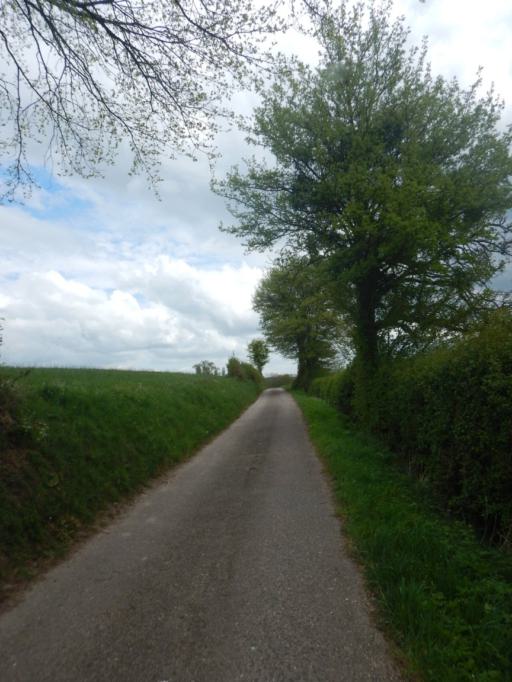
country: LU
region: Grevenmacher
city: Gonderange
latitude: 49.6872
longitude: 6.2793
